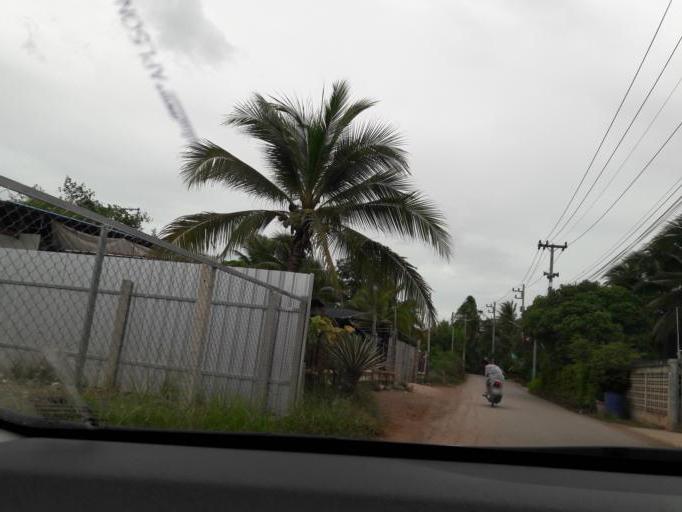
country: TH
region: Samut Sakhon
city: Ban Phaeo
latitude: 13.5485
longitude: 100.0396
